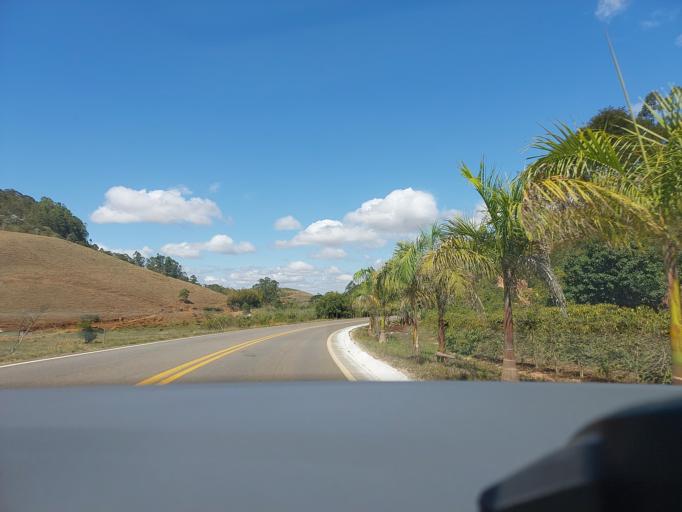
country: BR
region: Minas Gerais
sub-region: Mirai
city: Mirai
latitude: -21.0158
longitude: -42.5422
